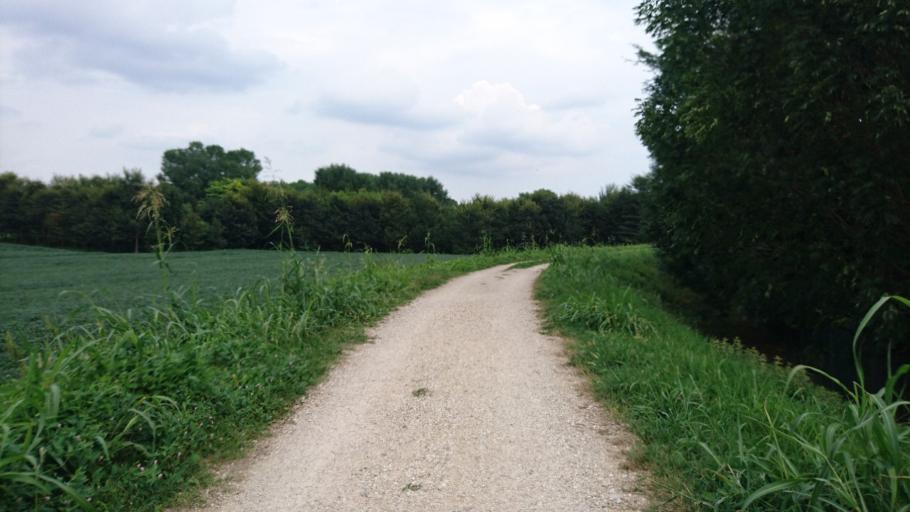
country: IT
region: Veneto
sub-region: Provincia di Padova
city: Saccolongo
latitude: 45.4050
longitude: 11.7497
